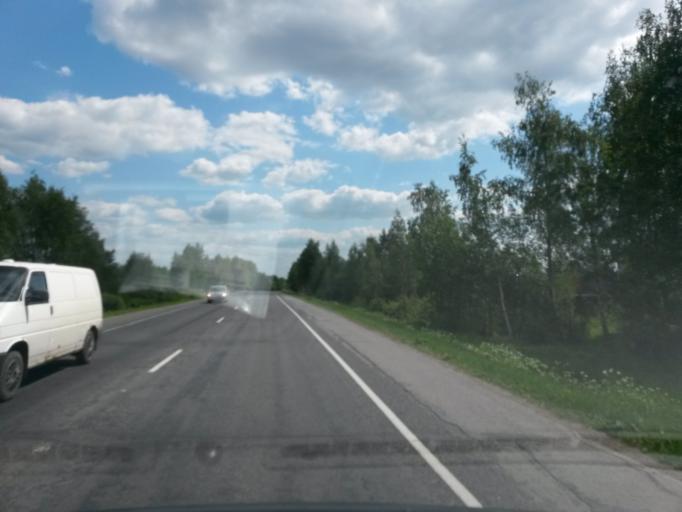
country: RU
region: Jaroslavl
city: Yaroslavl
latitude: 57.5561
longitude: 39.8696
